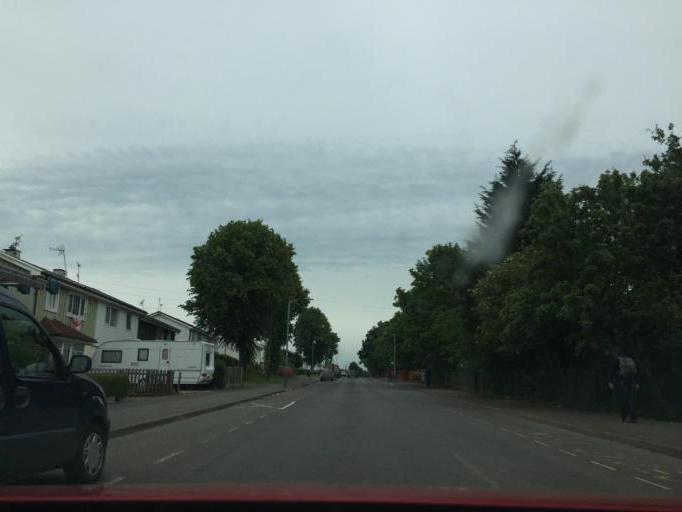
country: GB
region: England
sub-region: Warwickshire
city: Nuneaton
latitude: 52.5182
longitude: -1.4807
